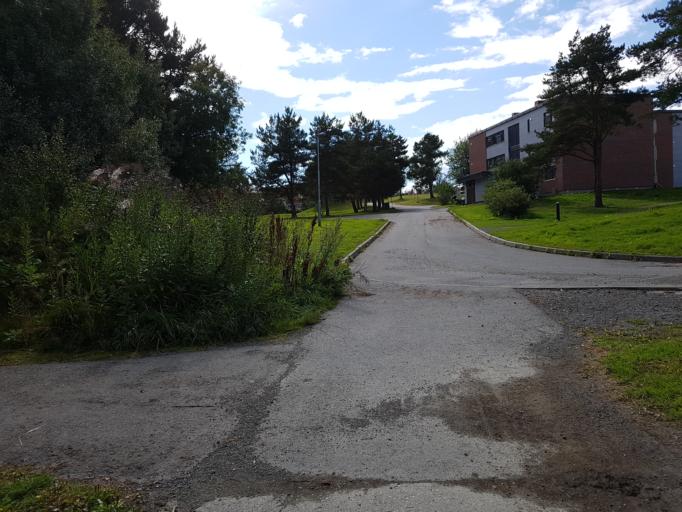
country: NO
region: Sor-Trondelag
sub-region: Trondheim
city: Trondheim
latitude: 63.4195
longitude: 10.4813
